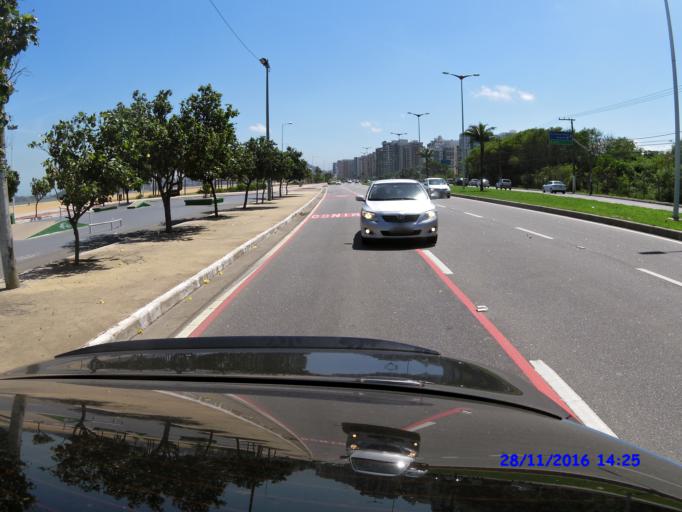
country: BR
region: Espirito Santo
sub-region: Vila Velha
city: Vila Velha
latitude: -20.2726
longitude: -40.2794
